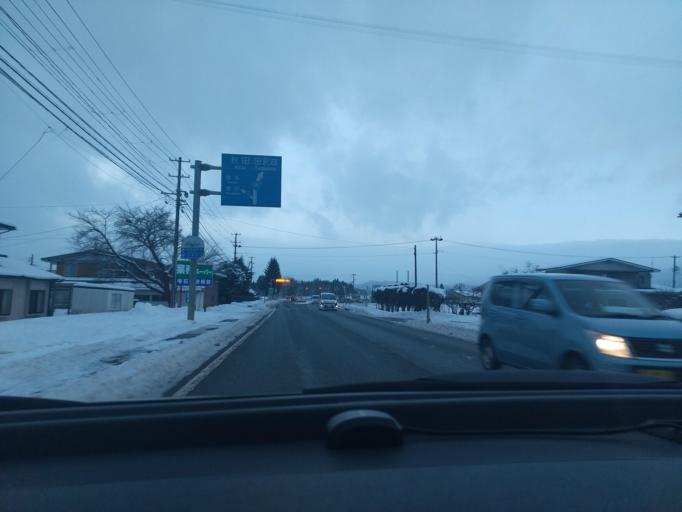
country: JP
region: Iwate
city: Shizukuishi
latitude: 39.6891
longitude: 140.9950
